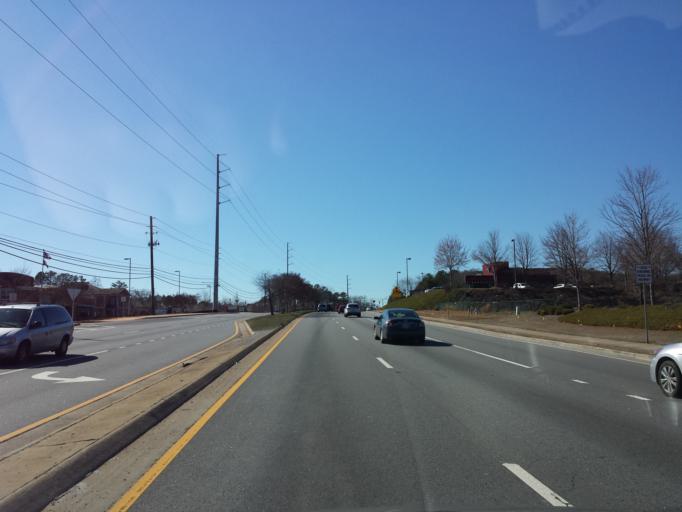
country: US
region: Georgia
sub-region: Cobb County
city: Marietta
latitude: 33.9464
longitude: -84.6270
